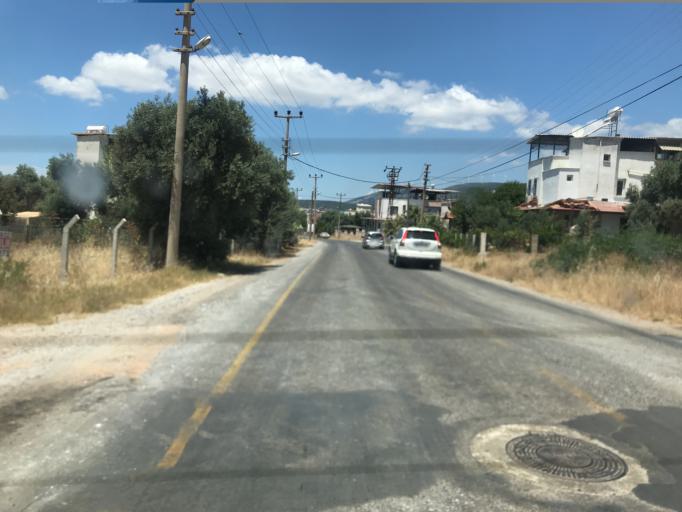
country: TR
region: Aydin
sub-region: Didim
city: Didim
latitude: 37.3990
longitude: 27.4377
